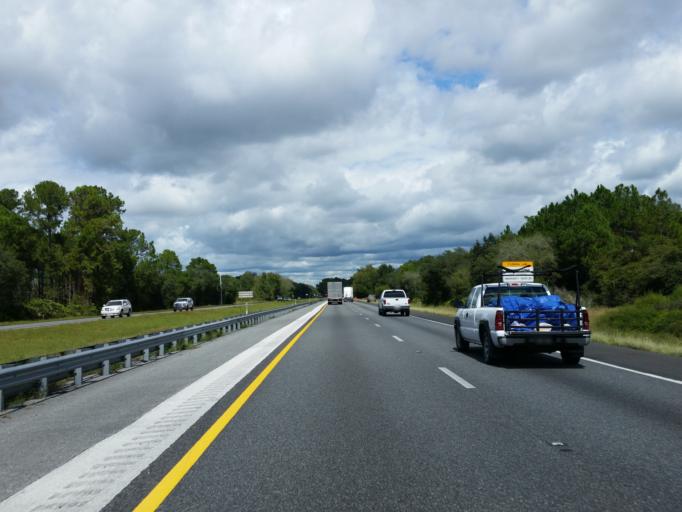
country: US
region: Florida
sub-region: Sumter County
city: Wildwood
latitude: 28.8435
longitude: -82.0905
